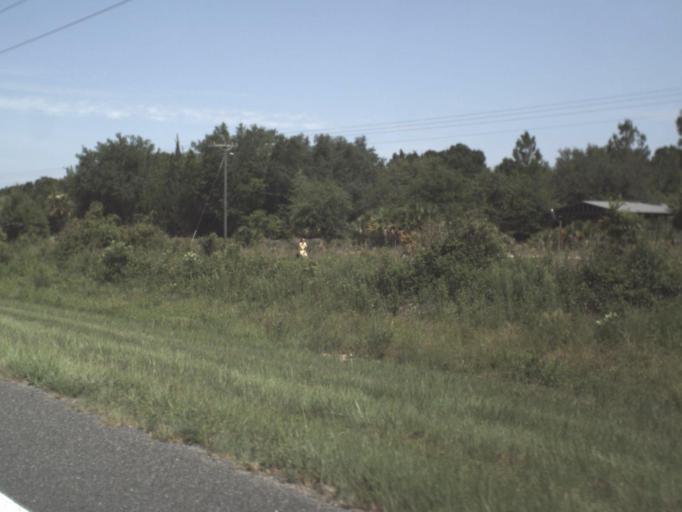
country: US
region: Florida
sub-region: Dixie County
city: Cross City
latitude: 29.6077
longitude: -83.0599
